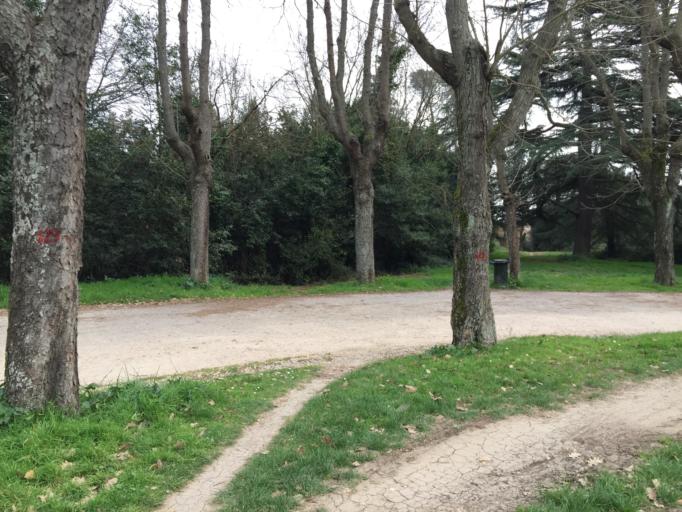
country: VA
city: Vatican City
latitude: 41.8825
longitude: 12.4474
